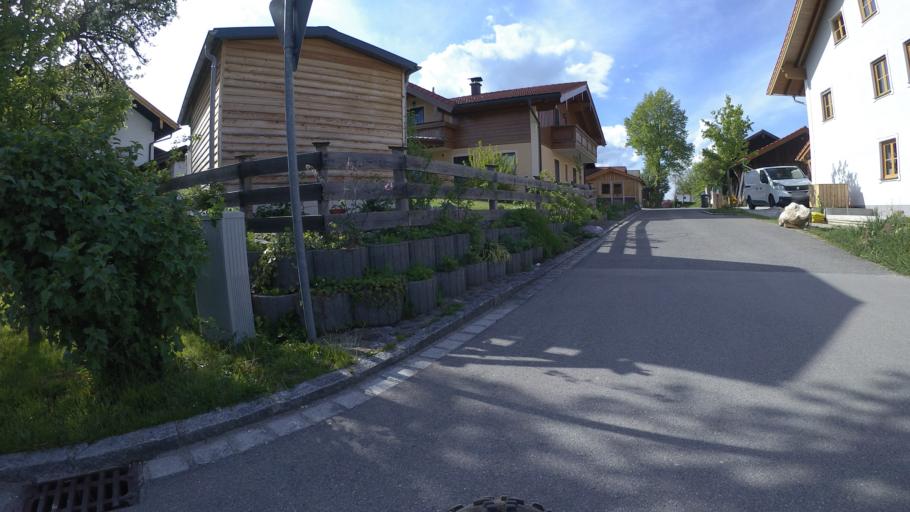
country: DE
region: Bavaria
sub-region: Upper Bavaria
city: Grabenstatt
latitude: 47.8442
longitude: 12.5448
